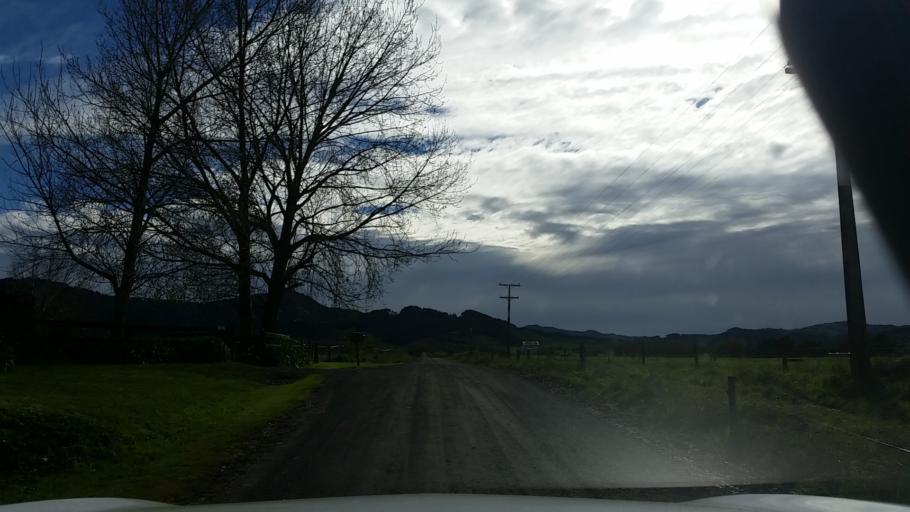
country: NZ
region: Waikato
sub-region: Hauraki District
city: Ngatea
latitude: -37.5157
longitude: 175.4105
